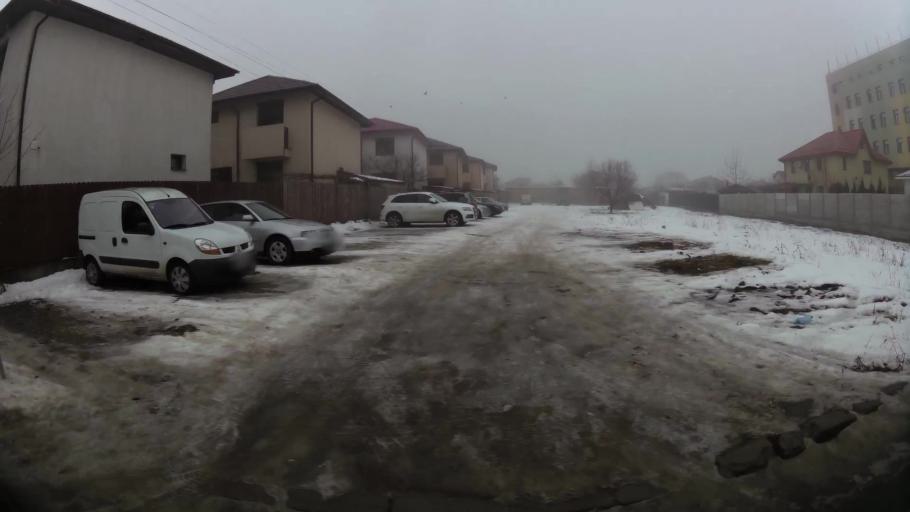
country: RO
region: Ilfov
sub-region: Comuna Chiajna
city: Chiajna
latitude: 44.4586
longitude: 25.9835
